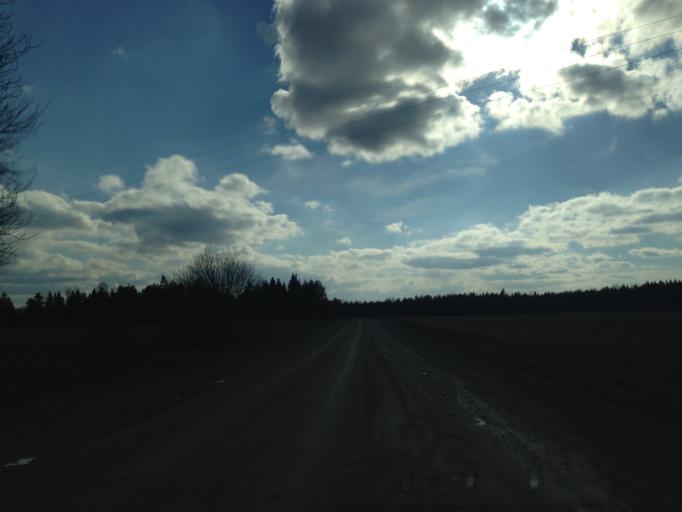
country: EE
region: Harju
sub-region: Nissi vald
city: Riisipere
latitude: 59.1235
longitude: 24.3611
